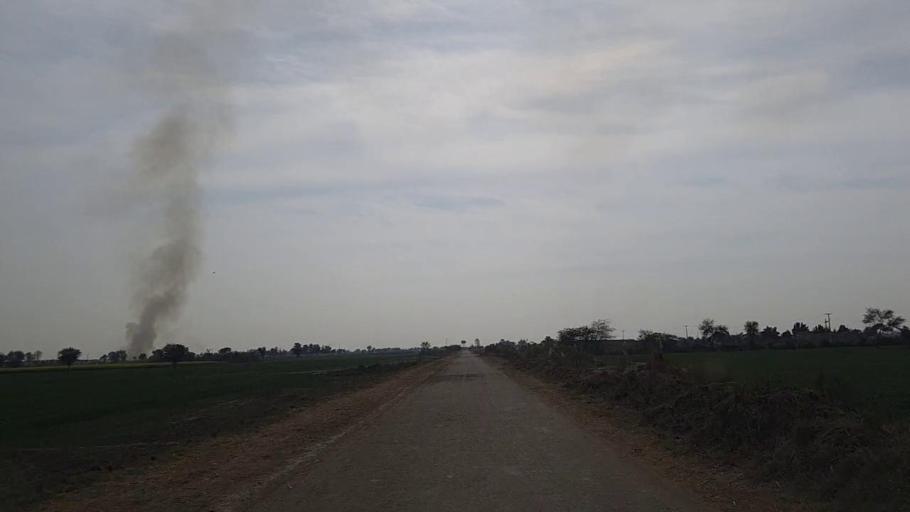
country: PK
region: Sindh
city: Daur
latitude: 26.4561
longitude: 68.4354
